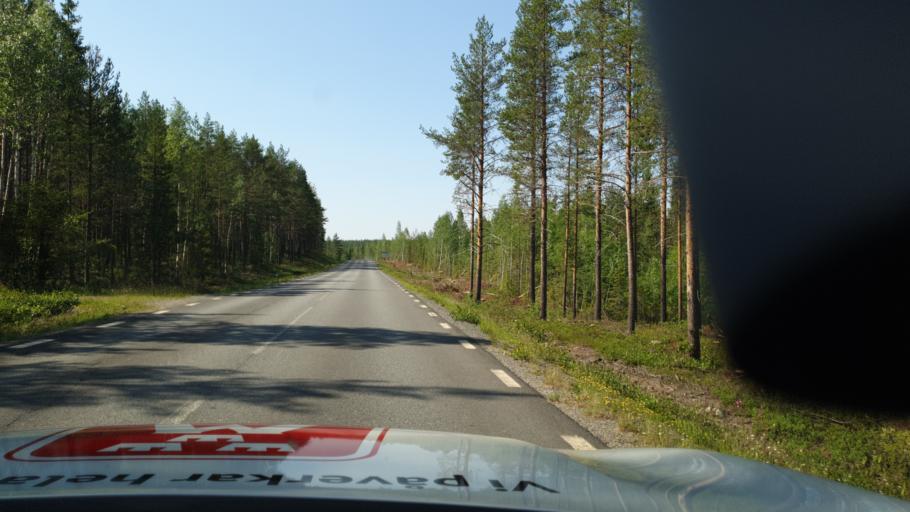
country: SE
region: Vaesterbotten
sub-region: Skelleftea Kommun
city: Langsele
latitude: 64.9515
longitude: 20.0289
